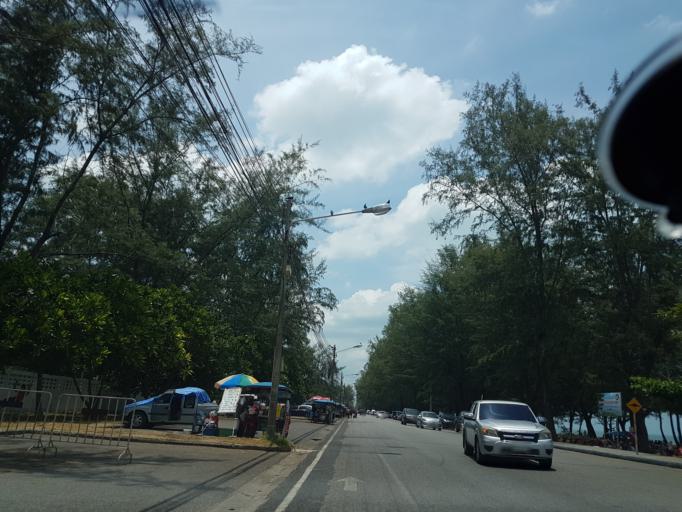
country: TH
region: Songkhla
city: Songkhla
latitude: 7.1978
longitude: 100.6059
